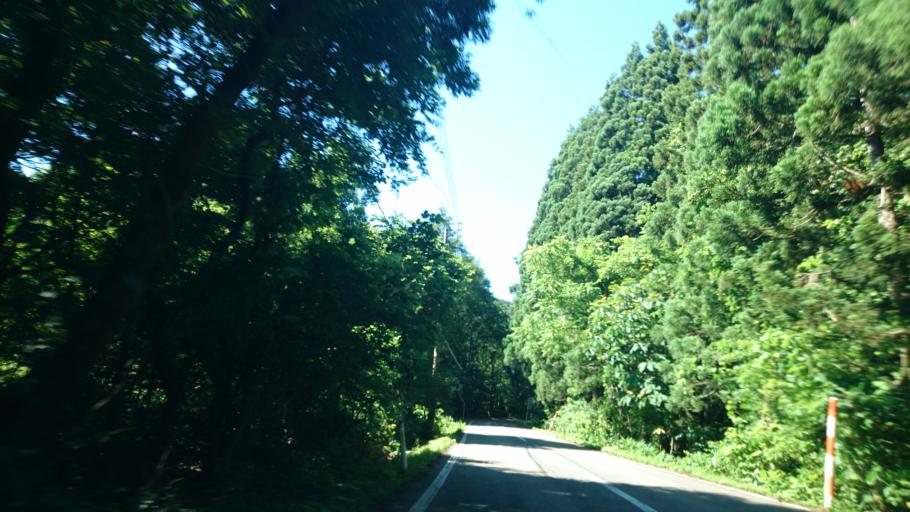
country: JP
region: Akita
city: Kakunodatemachi
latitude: 39.7241
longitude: 140.6987
